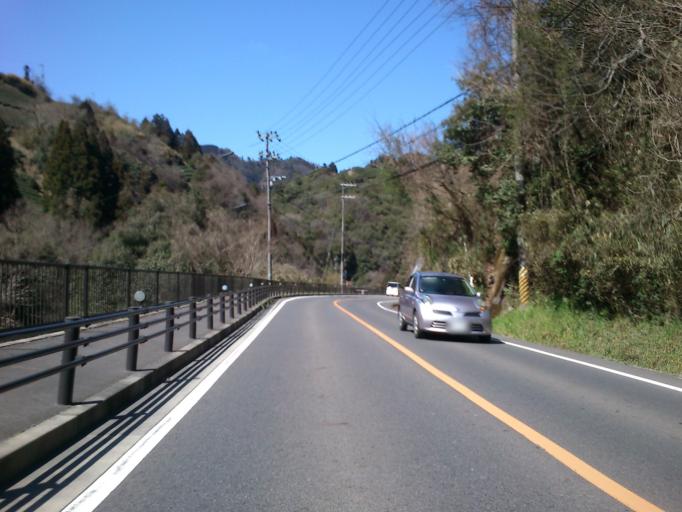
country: JP
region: Kyoto
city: Tanabe
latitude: 34.7872
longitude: 135.8864
